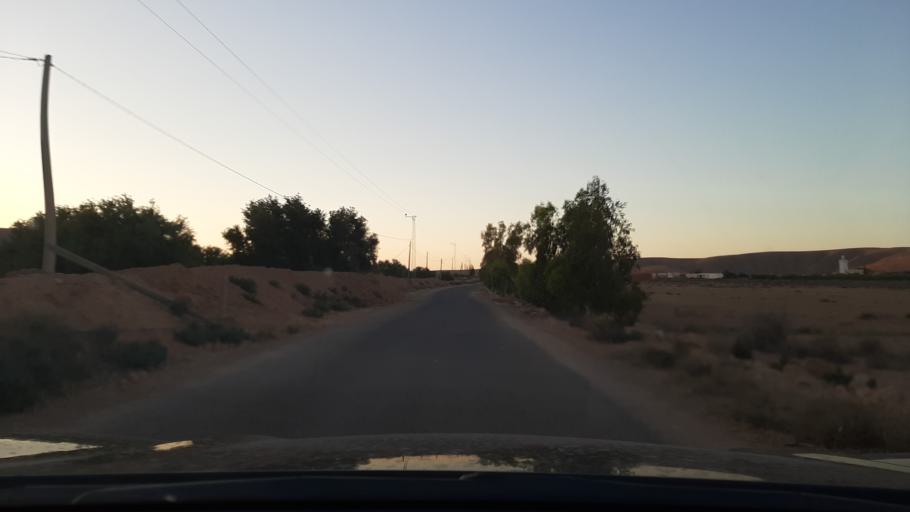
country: TN
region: Qabis
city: Matmata
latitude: 33.5656
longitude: 10.1789
